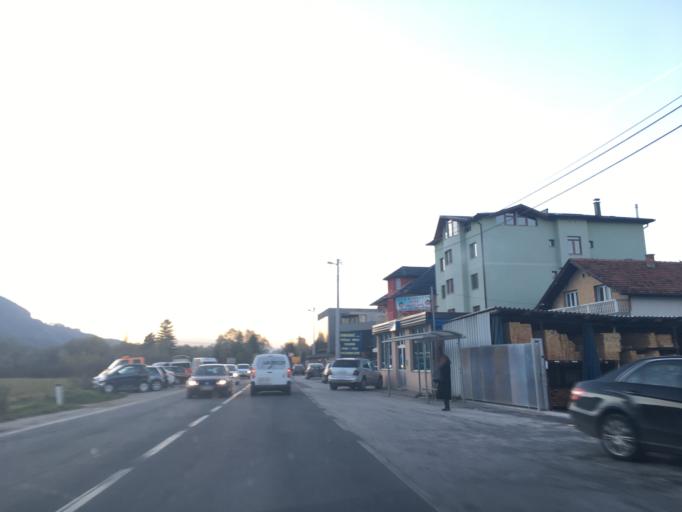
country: BA
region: Federation of Bosnia and Herzegovina
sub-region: Kanton Sarajevo
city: Sarajevo
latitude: 43.8309
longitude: 18.2914
